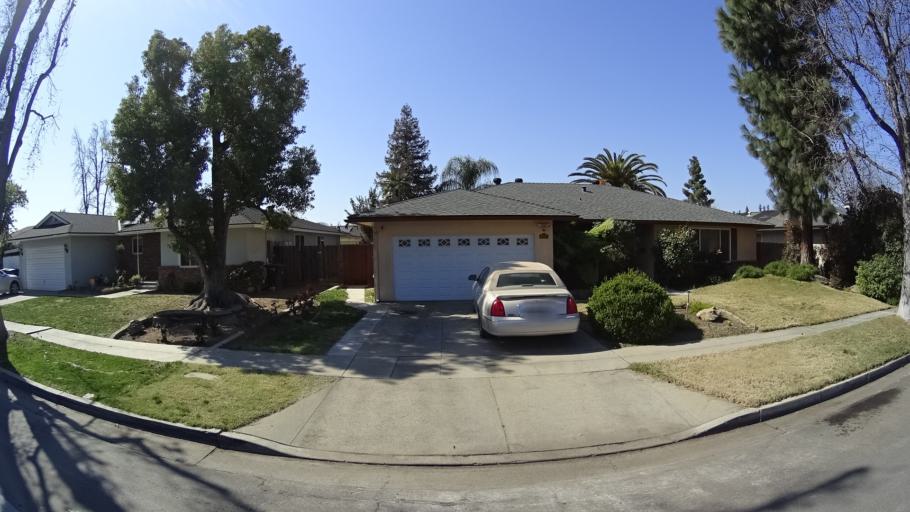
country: US
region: California
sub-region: Fresno County
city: Clovis
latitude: 36.8328
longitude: -119.7792
